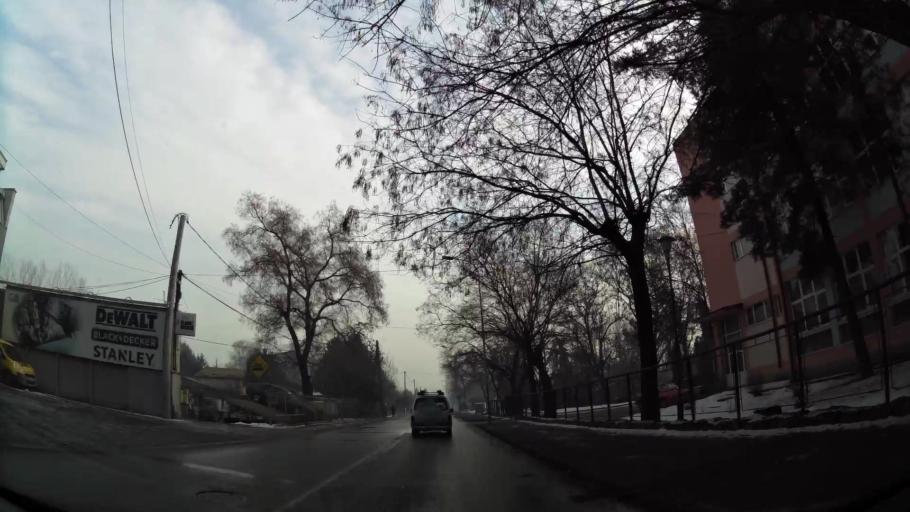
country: MK
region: Cair
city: Cair
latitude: 42.0027
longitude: 21.4801
